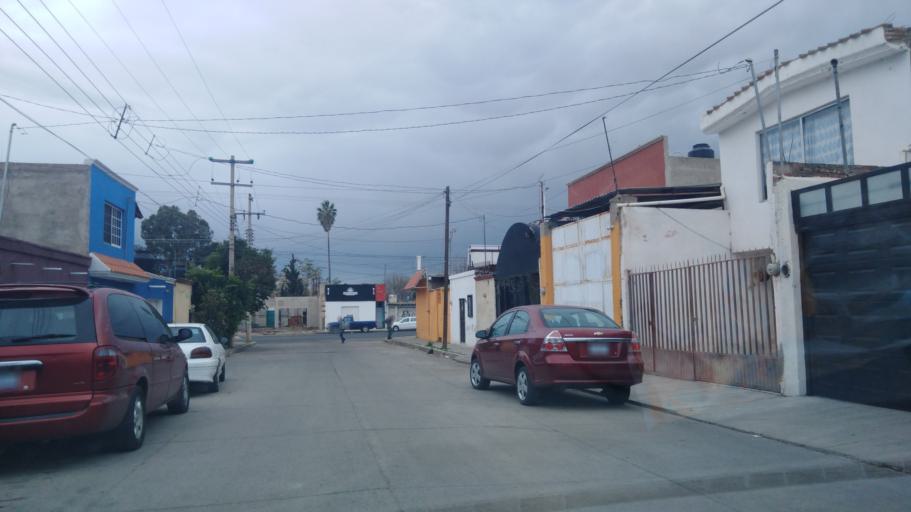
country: MX
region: Durango
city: Victoria de Durango
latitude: 24.0392
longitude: -104.6698
